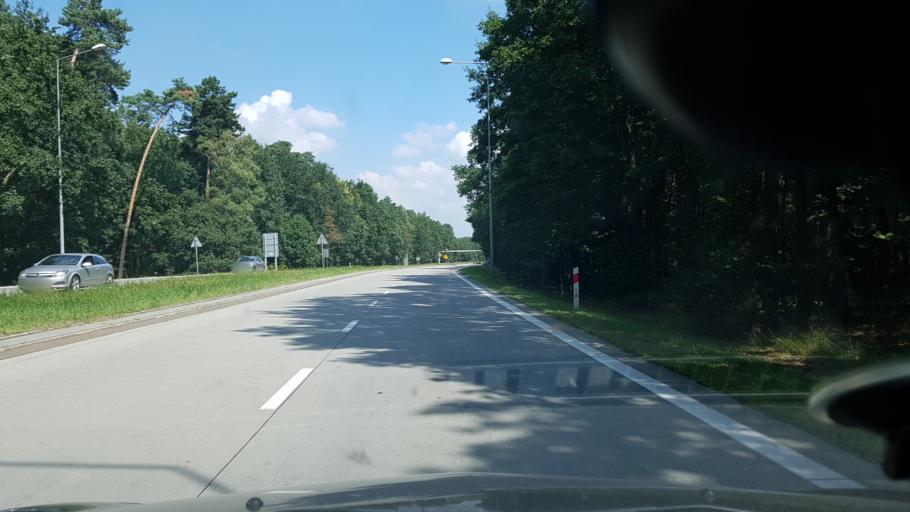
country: PL
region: Silesian Voivodeship
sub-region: Zory
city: Zory
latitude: 50.0633
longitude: 18.7251
